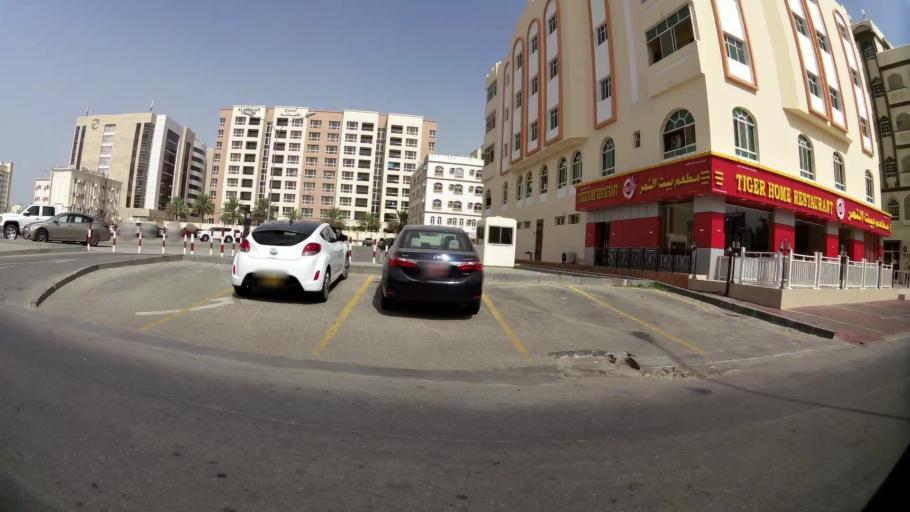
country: OM
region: Muhafazat Masqat
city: Bawshar
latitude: 23.5821
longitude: 58.3961
